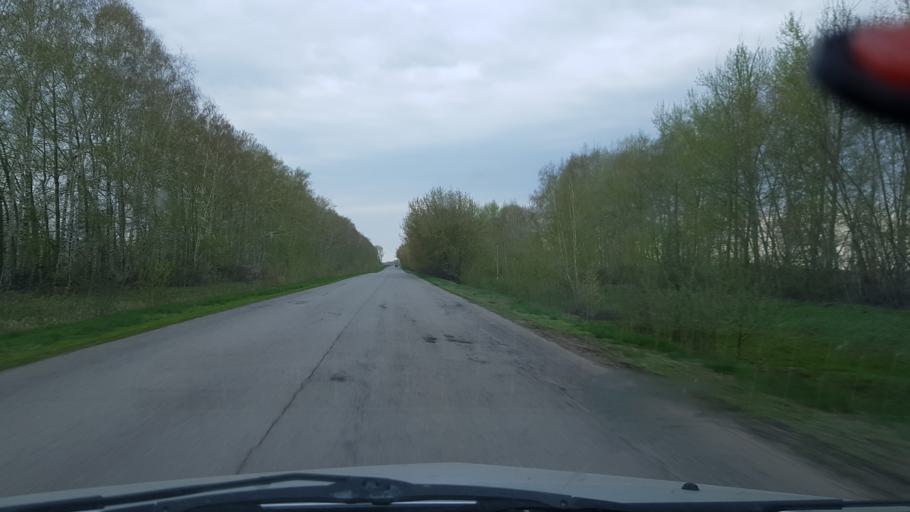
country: RU
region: Samara
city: Podstepki
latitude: 53.6646
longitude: 49.1782
